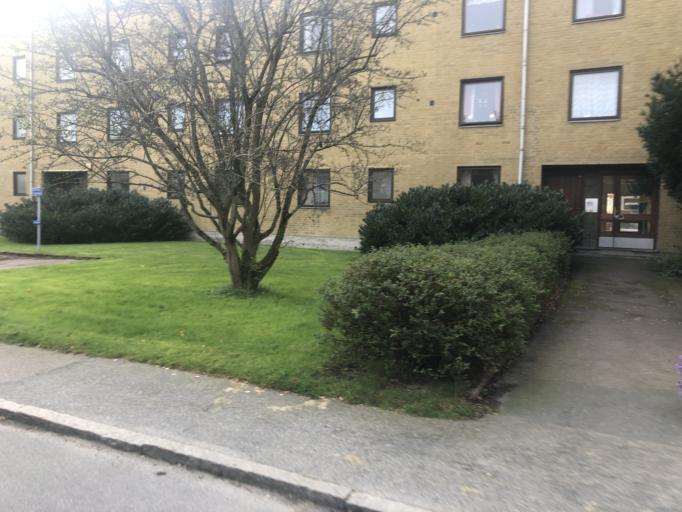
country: SE
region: Vaestra Goetaland
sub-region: Molndal
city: Moelndal
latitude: 57.6501
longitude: 12.0145
